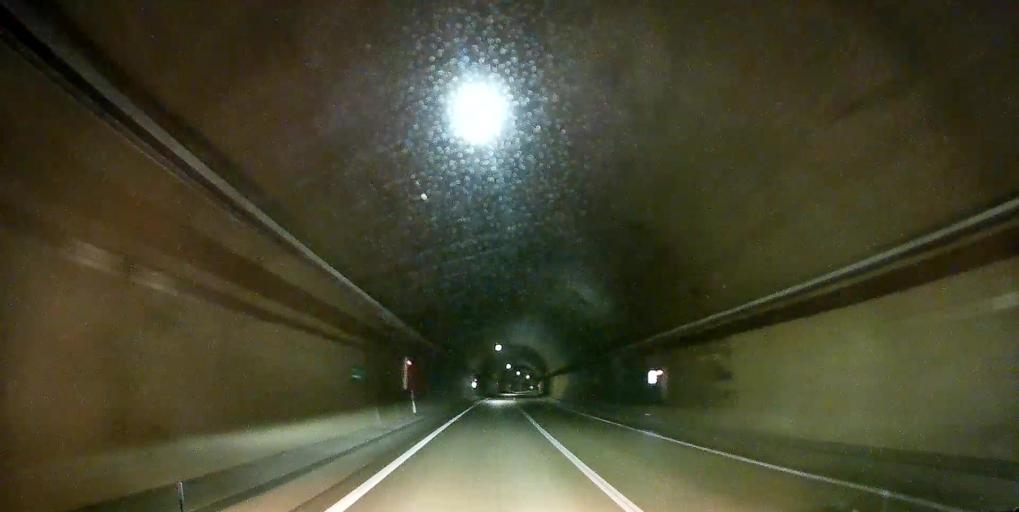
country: JP
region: Hokkaido
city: Iwanai
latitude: 42.3046
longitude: 139.7731
